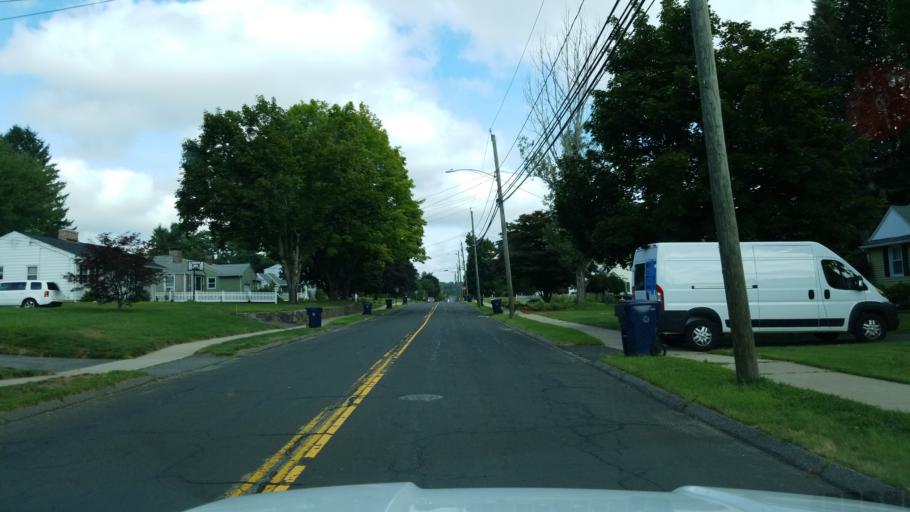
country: US
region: Connecticut
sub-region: Litchfield County
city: Terryville
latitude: 41.6720
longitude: -72.9988
